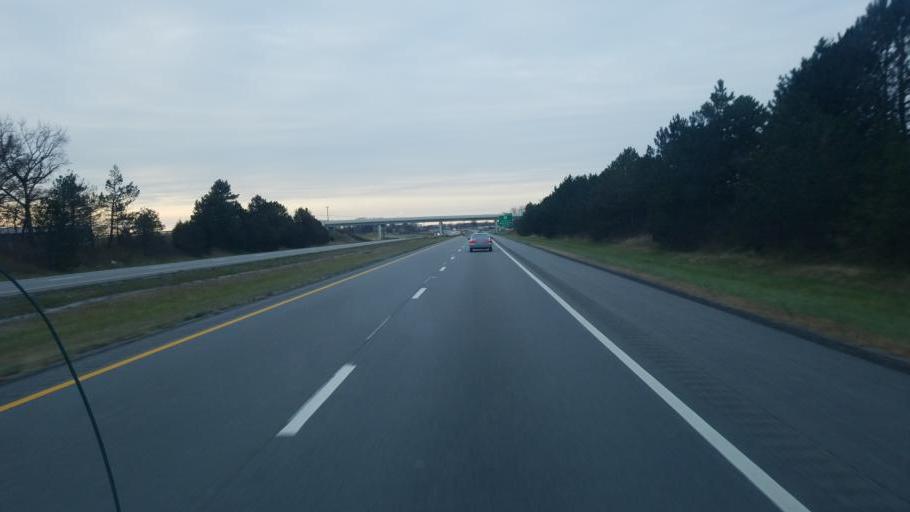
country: US
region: Ohio
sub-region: Auglaize County
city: Cridersville
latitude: 40.6086
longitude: -84.1525
